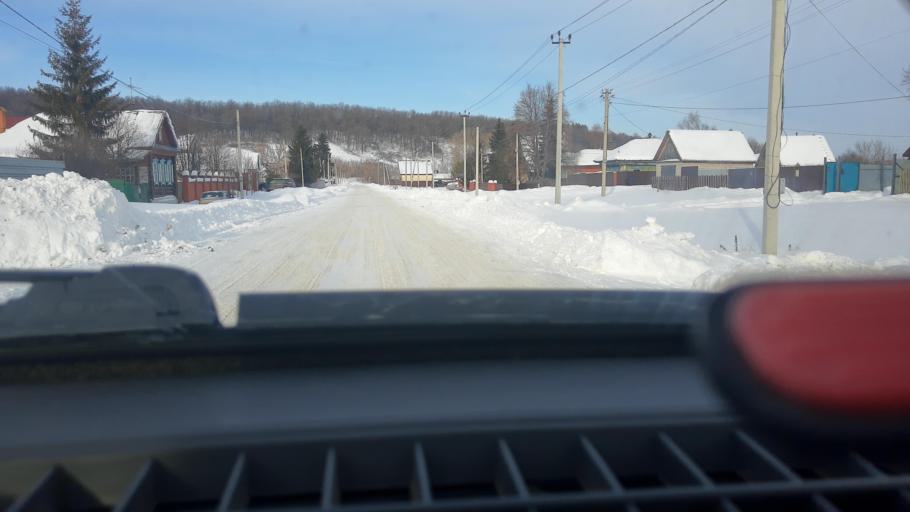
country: RU
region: Bashkortostan
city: Ufa
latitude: 54.5208
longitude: 55.9110
